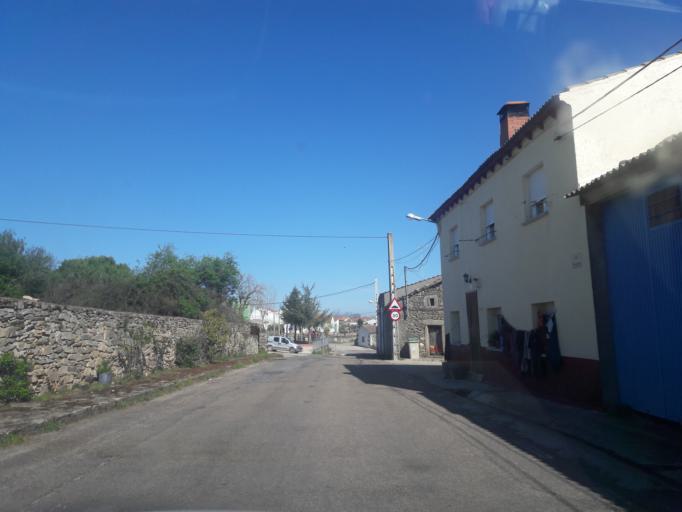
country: ES
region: Castille and Leon
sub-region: Provincia de Salamanca
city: Valsalabroso
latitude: 41.1516
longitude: -6.4870
